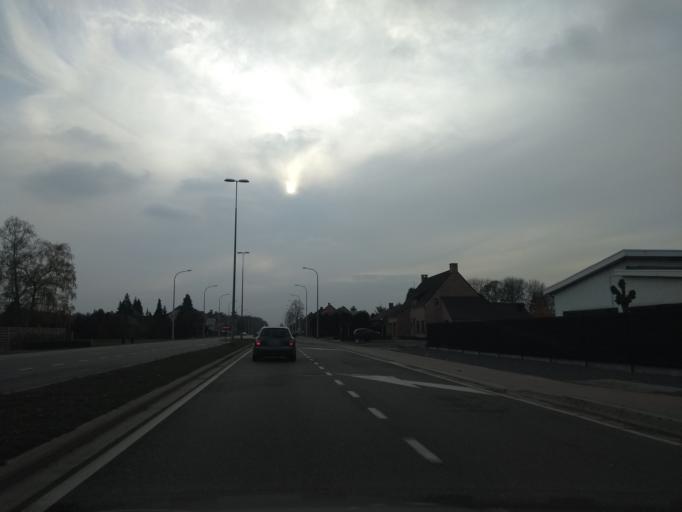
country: NL
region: Limburg
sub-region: Gemeente Stein
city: Berg
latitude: 51.0434
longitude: 5.7340
